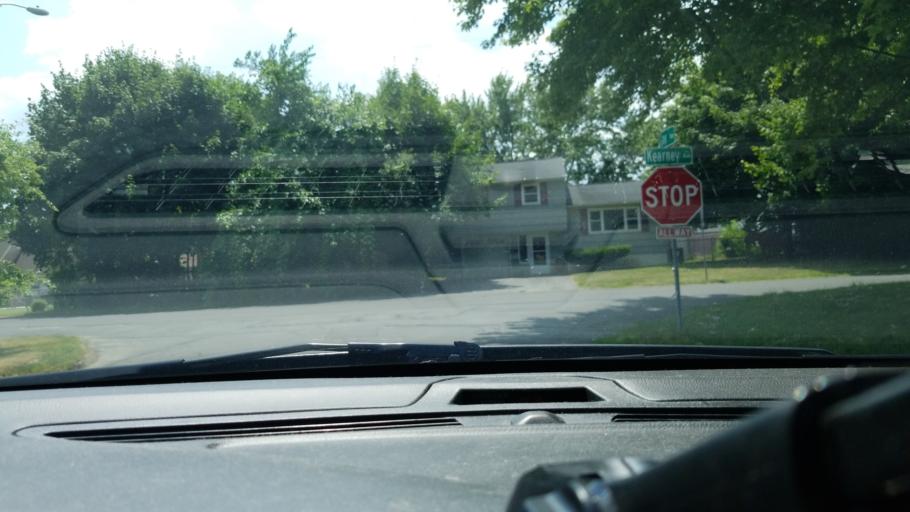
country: US
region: New York
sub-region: Onondaga County
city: Galeville
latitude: 43.0876
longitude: -76.1707
